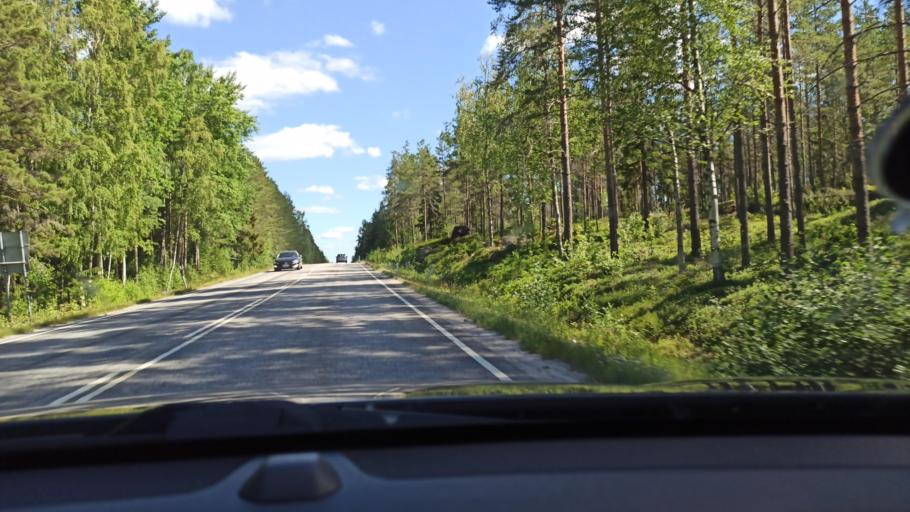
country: FI
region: Ostrobothnia
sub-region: Vaasa
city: Malax
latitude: 62.9870
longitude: 21.6353
